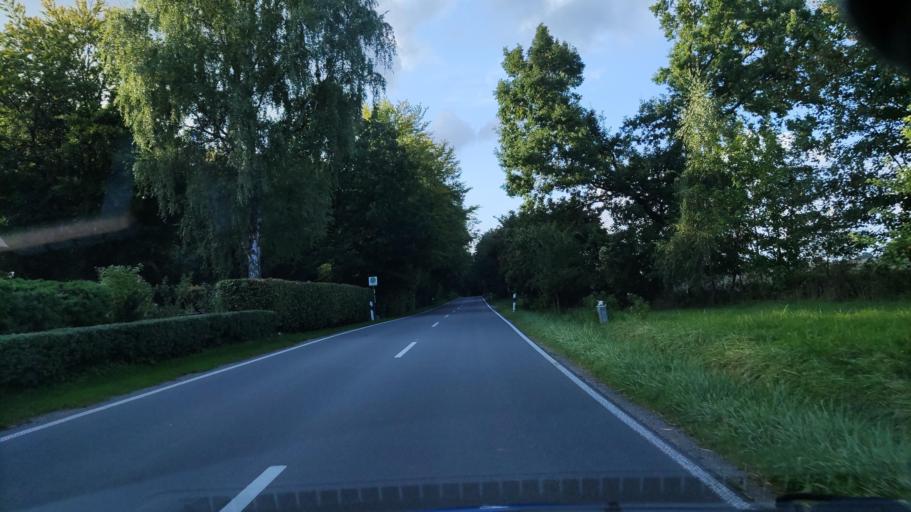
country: DE
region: Schleswig-Holstein
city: Ahrensbok
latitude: 54.0307
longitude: 10.5550
